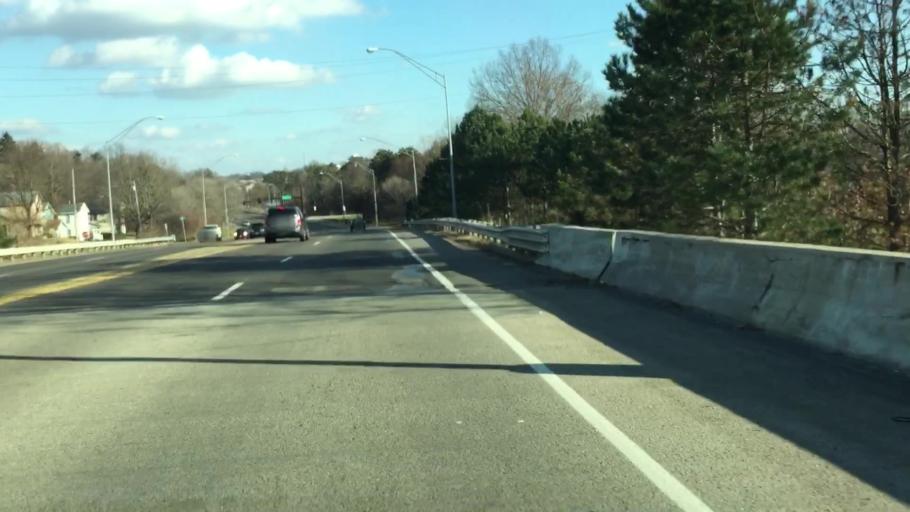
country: US
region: Ohio
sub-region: Portage County
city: Kent
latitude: 41.1507
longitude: -81.3721
